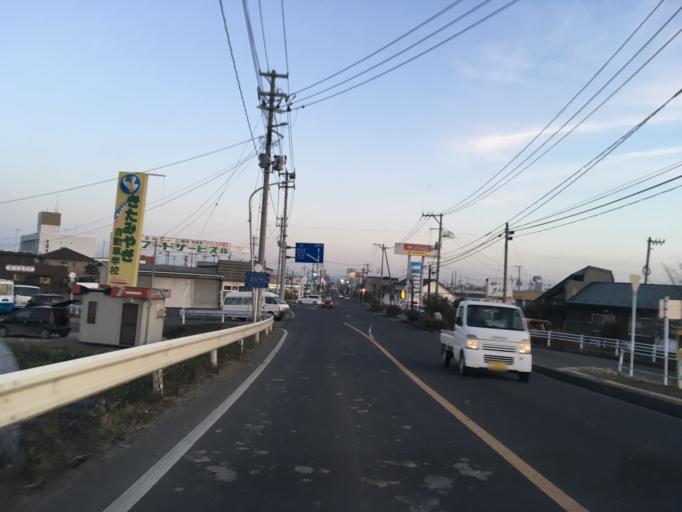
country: JP
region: Miyagi
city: Wakuya
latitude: 38.6912
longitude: 141.1795
